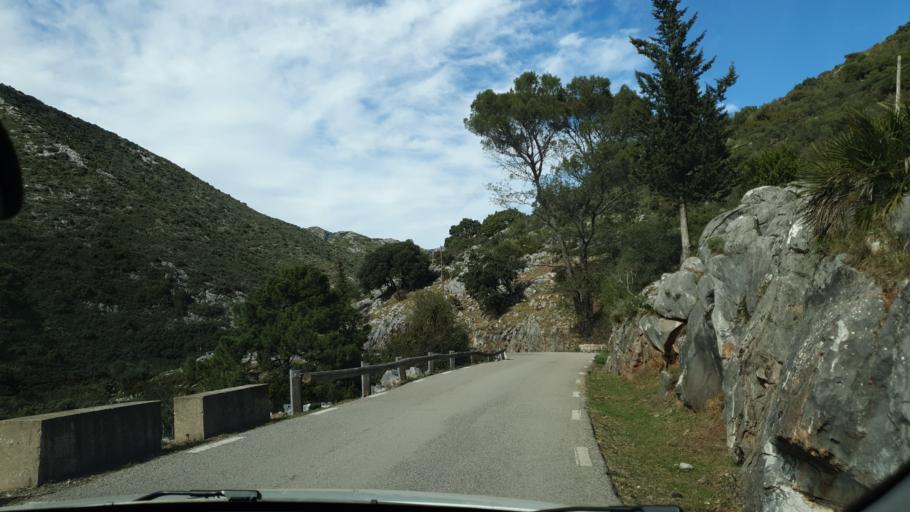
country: ES
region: Andalusia
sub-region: Provincia de Malaga
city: Ojen
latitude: 36.5814
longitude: -4.8841
